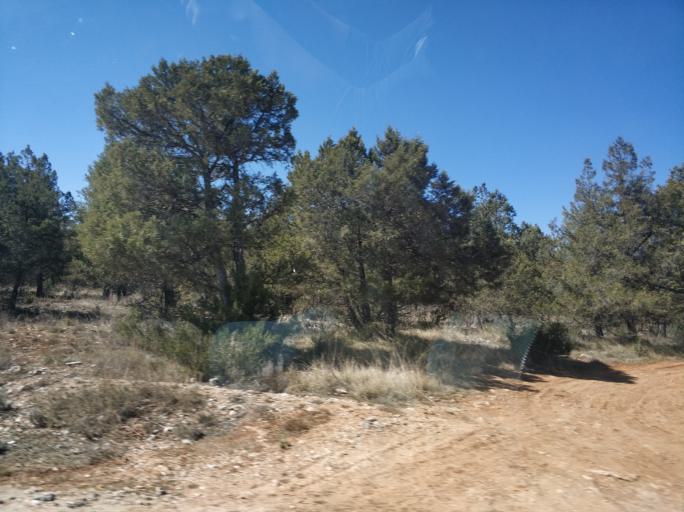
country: ES
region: Castille and Leon
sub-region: Provincia de Soria
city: Ucero
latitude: 41.7385
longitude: -3.0444
